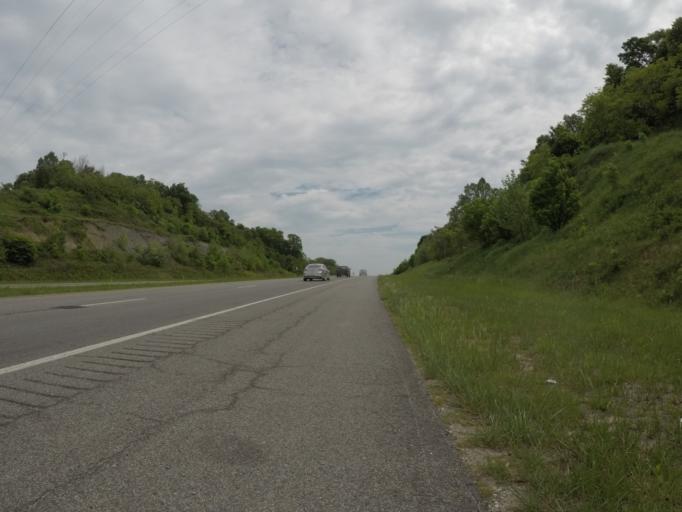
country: US
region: West Virginia
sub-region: Wayne County
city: Kenova
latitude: 38.3772
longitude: -82.5856
